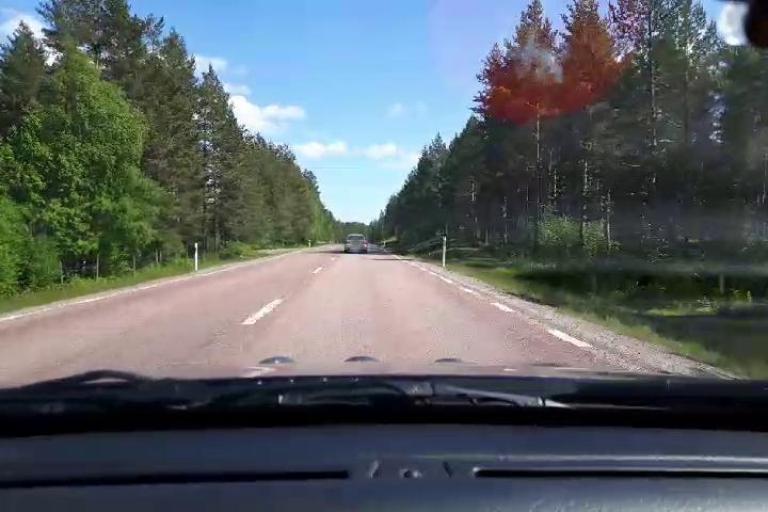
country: SE
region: Gaevleborg
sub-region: Hudiksvalls Kommun
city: Sorforsa
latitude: 61.7554
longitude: 16.8171
